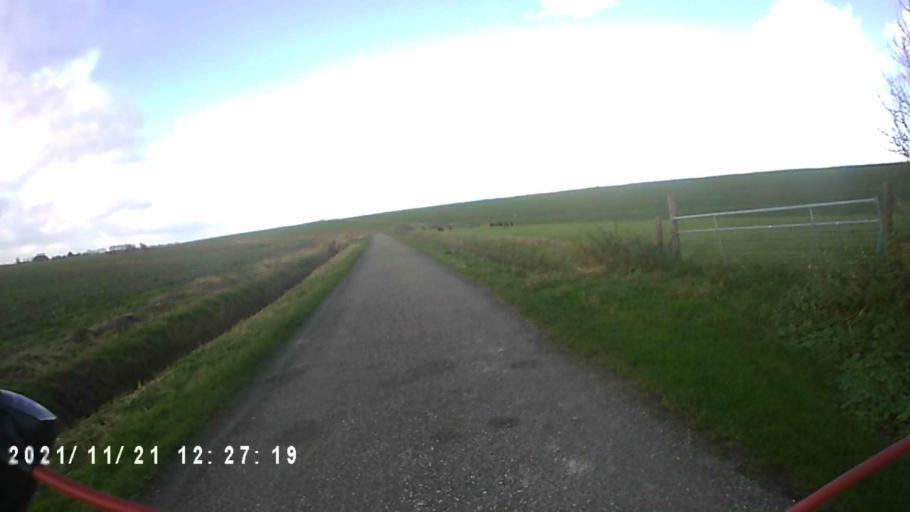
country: NL
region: Friesland
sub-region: Gemeente Dongeradeel
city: Anjum
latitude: 53.4042
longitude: 6.0544
